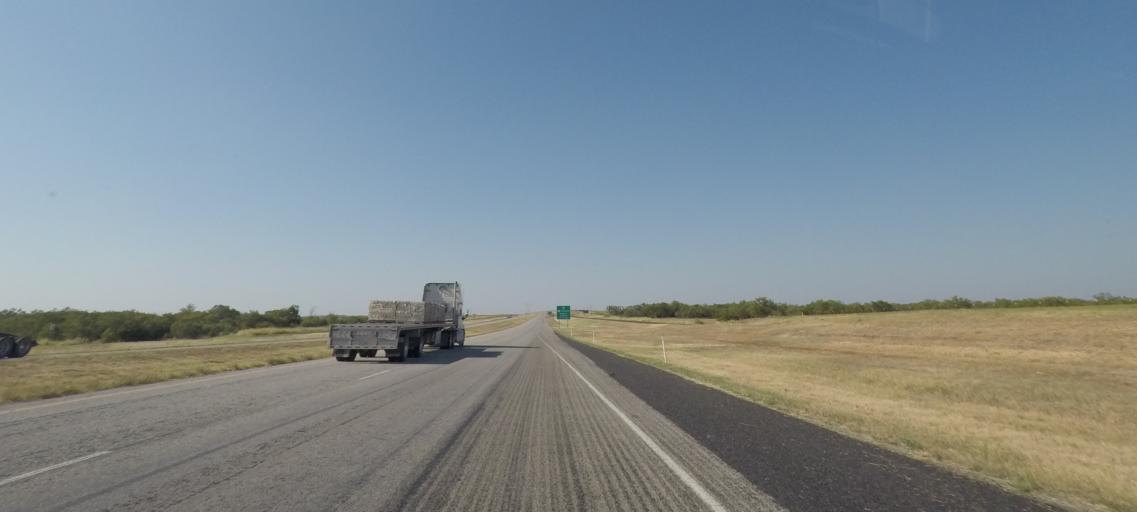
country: US
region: Texas
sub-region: Baylor County
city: Seymour
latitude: 33.6038
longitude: -99.2420
